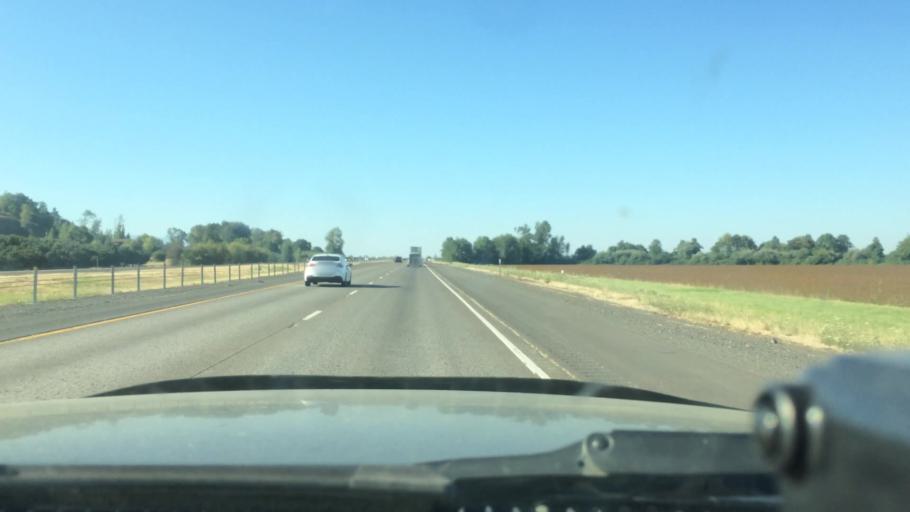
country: US
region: Oregon
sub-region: Linn County
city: Tangent
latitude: 44.4608
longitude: -123.0617
